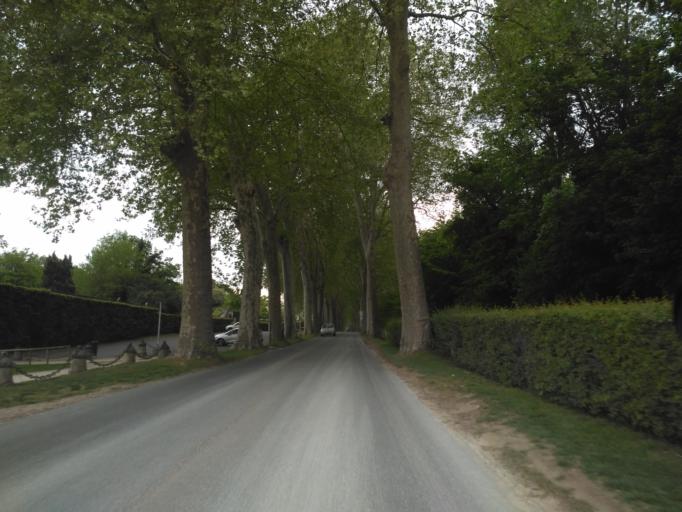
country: FR
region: Ile-de-France
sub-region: Departement de Seine-et-Marne
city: Maincy
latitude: 48.5684
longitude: 2.7129
